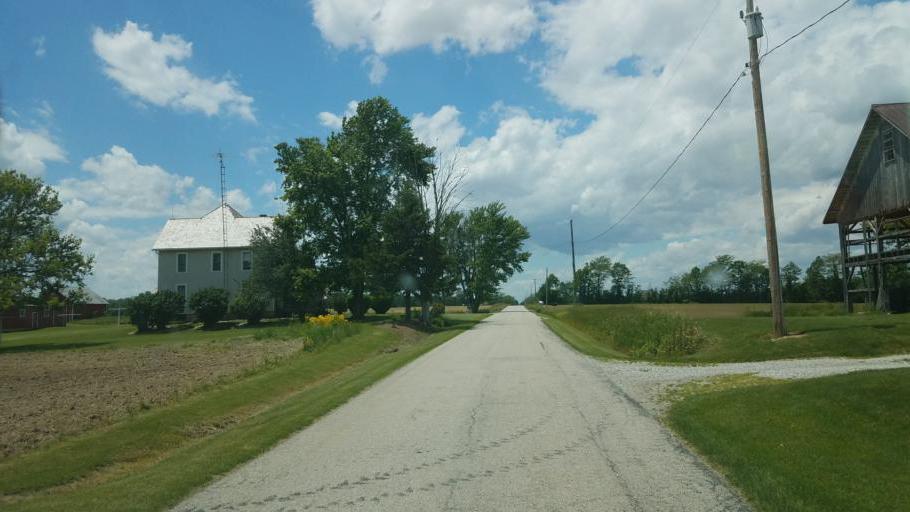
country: US
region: Ohio
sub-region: Huron County
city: Willard
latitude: 41.1426
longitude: -82.7689
